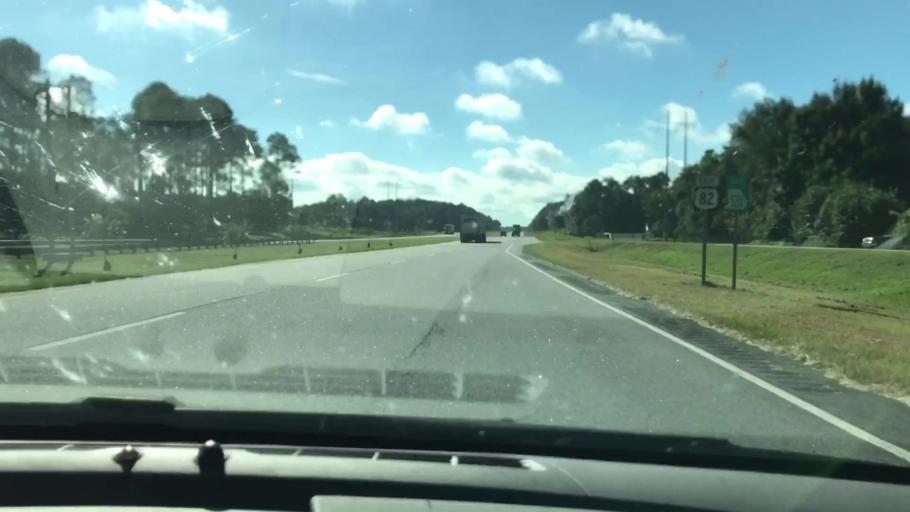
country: US
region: Georgia
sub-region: Dougherty County
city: Albany
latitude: 31.5708
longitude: -84.0256
